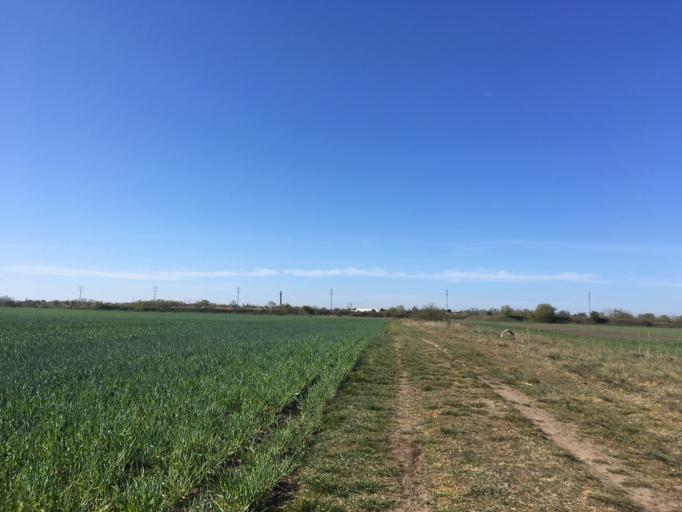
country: DE
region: Berlin
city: Buchholz
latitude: 52.6255
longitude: 13.4453
